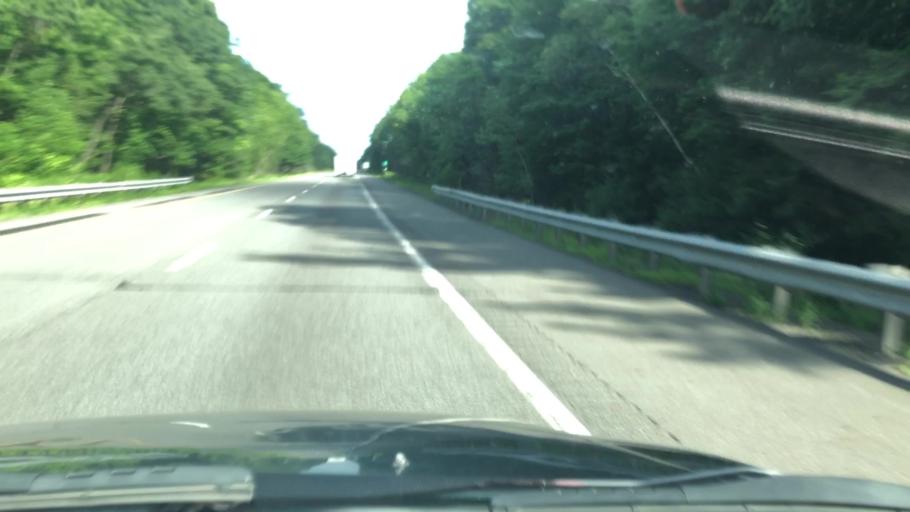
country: US
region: Pennsylvania
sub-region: Pike County
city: Milford
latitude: 41.3384
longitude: -74.8692
